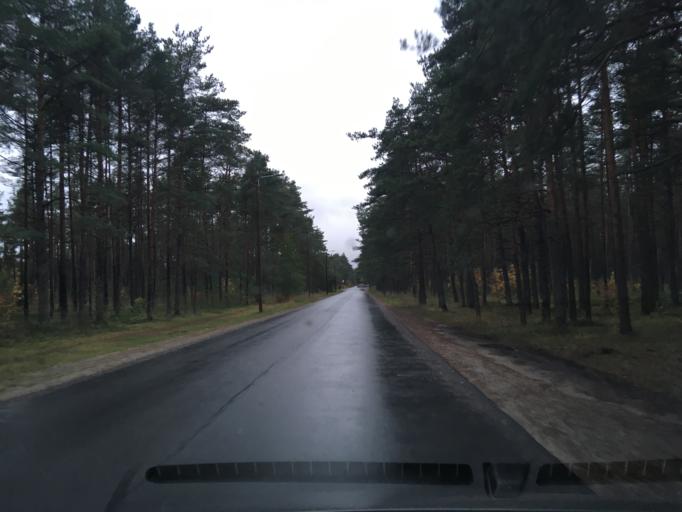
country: EE
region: Harju
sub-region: Saue vald
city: Laagri
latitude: 59.3776
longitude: 24.6813
